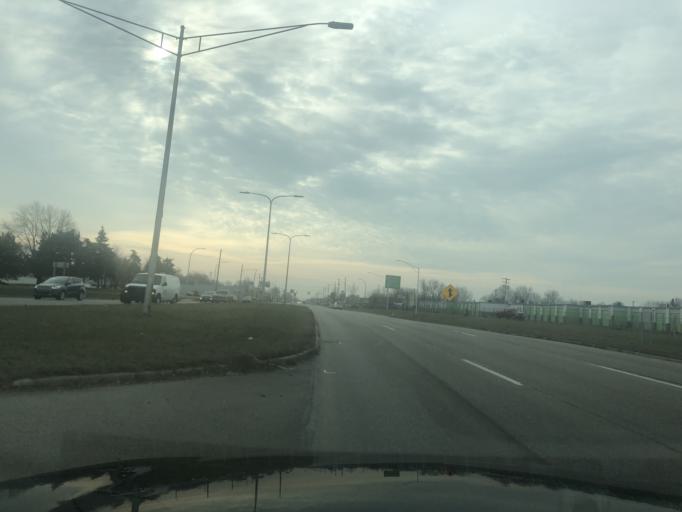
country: US
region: Michigan
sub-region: Wayne County
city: Lincoln Park
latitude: 42.2418
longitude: -83.1951
